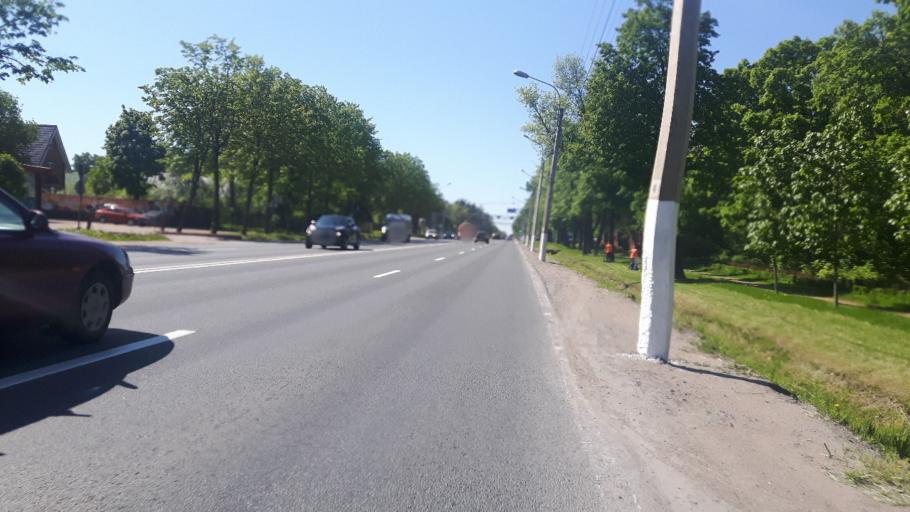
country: RU
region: Leningrad
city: Ol'gino
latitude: 59.8742
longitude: 29.9502
